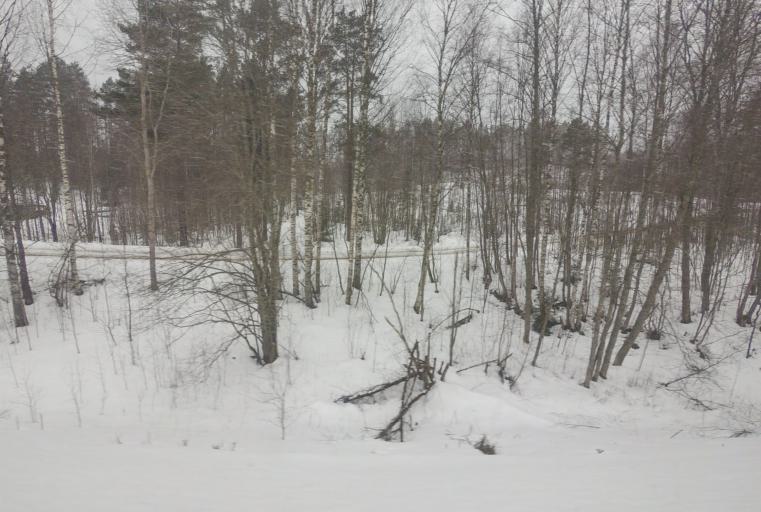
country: FI
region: Southern Savonia
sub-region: Savonlinna
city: Punkaharju
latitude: 61.6636
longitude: 29.4134
